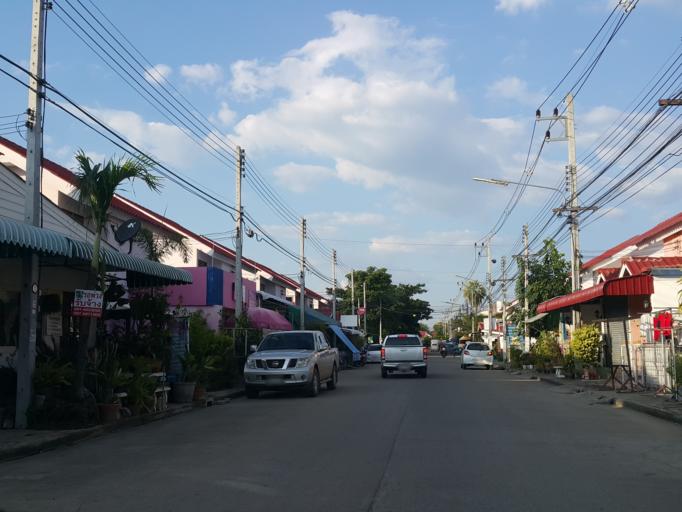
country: TH
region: Chiang Mai
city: San Kamphaeng
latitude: 18.7462
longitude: 99.0871
